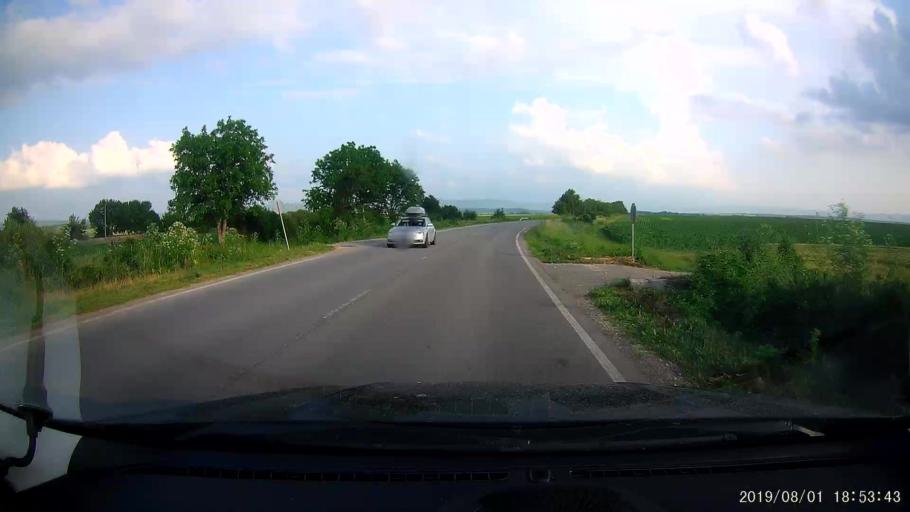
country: BG
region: Shumen
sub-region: Obshtina Shumen
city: Shumen
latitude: 43.2162
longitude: 26.9971
